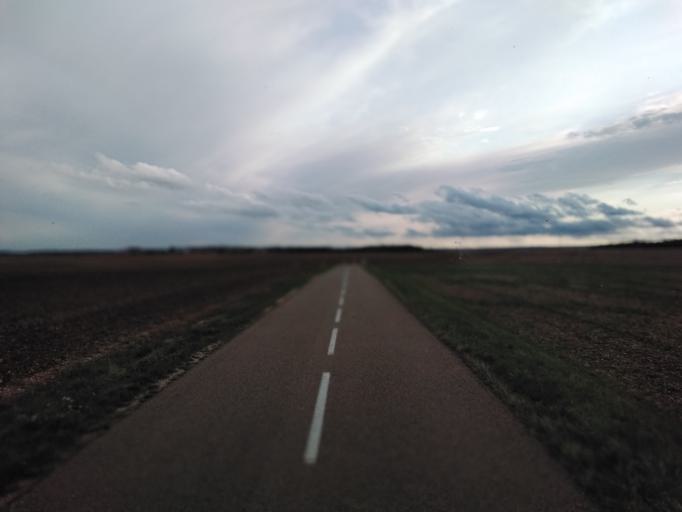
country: FR
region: Bourgogne
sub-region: Departement de l'Yonne
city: Ravieres
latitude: 47.7609
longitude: 4.3560
